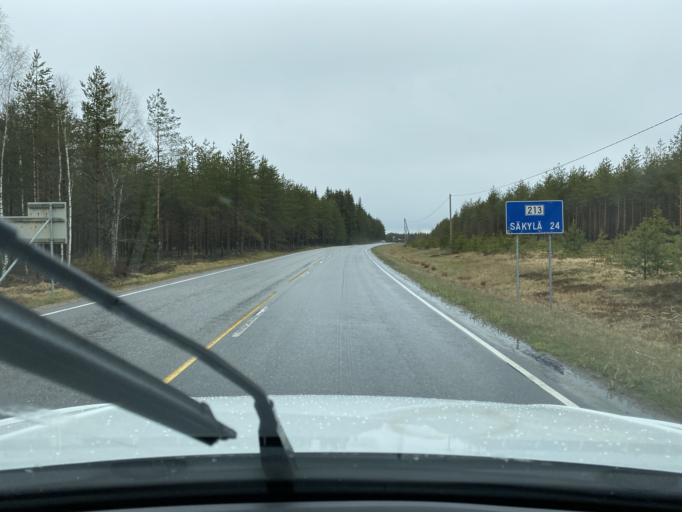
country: FI
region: Satakunta
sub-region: Pori
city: Vampula
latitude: 60.9514
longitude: 22.6744
